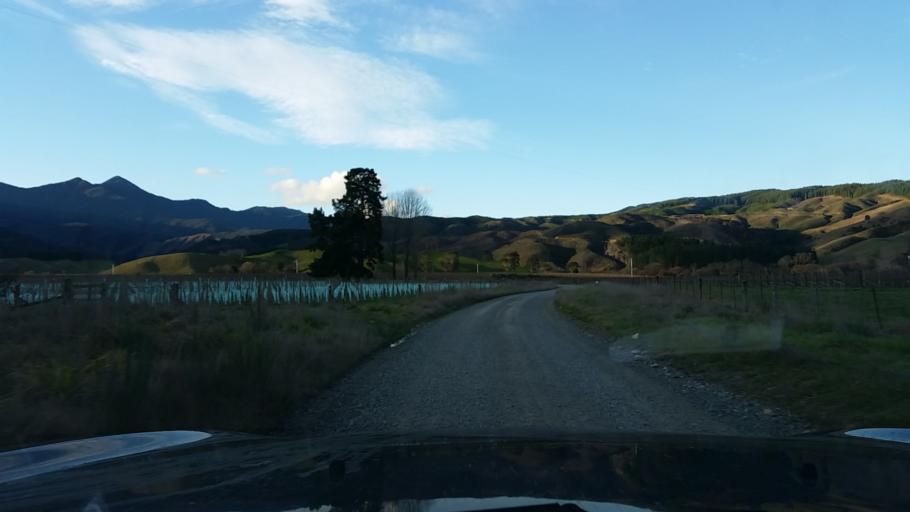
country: NZ
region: Marlborough
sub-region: Marlborough District
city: Blenheim
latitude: -41.5176
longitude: 173.5841
